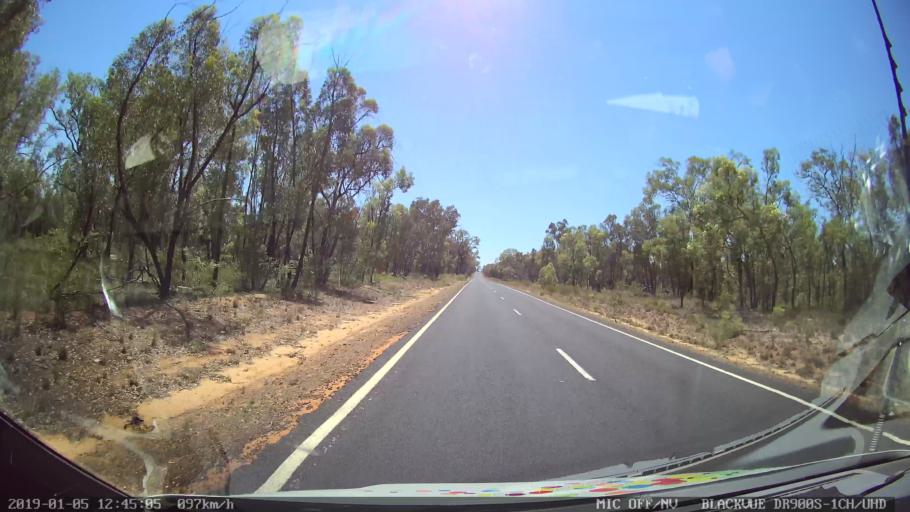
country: AU
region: New South Wales
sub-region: Warrumbungle Shire
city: Coonabarabran
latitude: -31.1313
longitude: 149.5455
